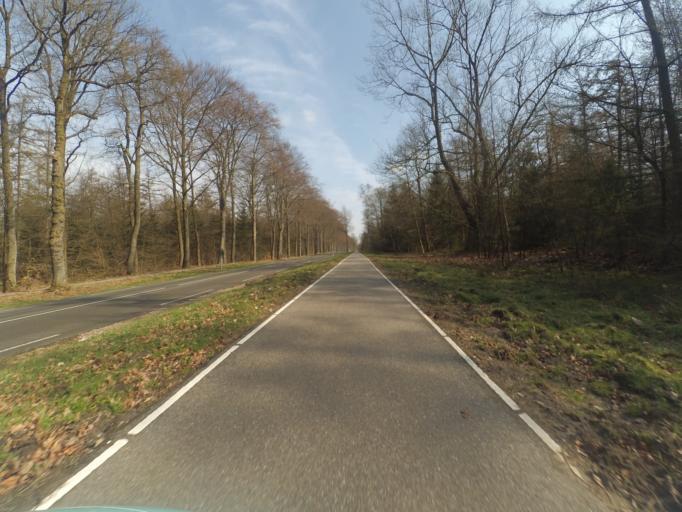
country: NL
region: Gelderland
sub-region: Gemeente Apeldoorn
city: Beekbergen
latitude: 52.1542
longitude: 5.8897
